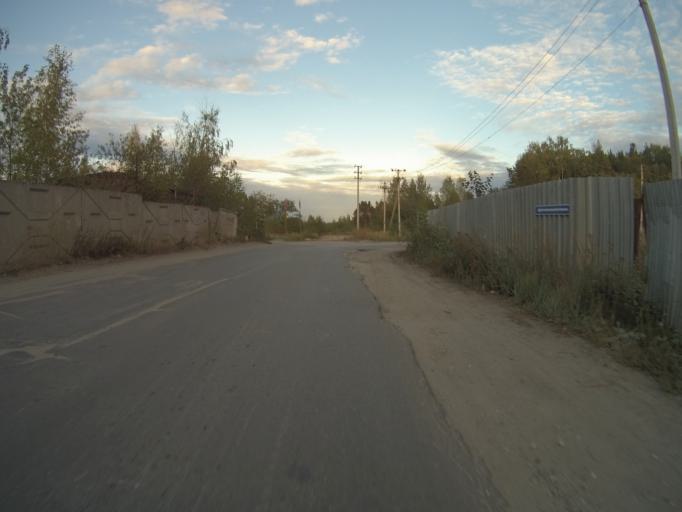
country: RU
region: Vladimir
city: Vladimir
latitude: 56.0929
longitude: 40.3696
